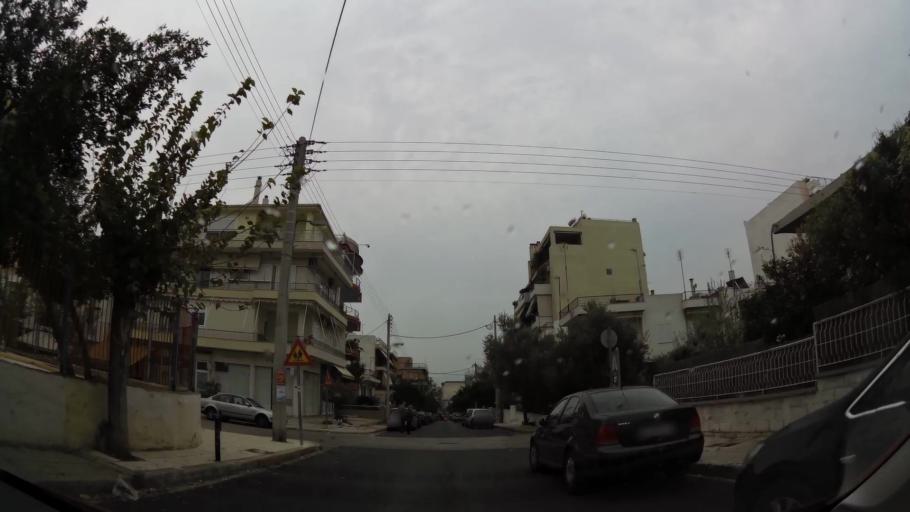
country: GR
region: Attica
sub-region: Nomarchia Athinas
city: Peristeri
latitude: 38.0173
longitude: 23.7029
